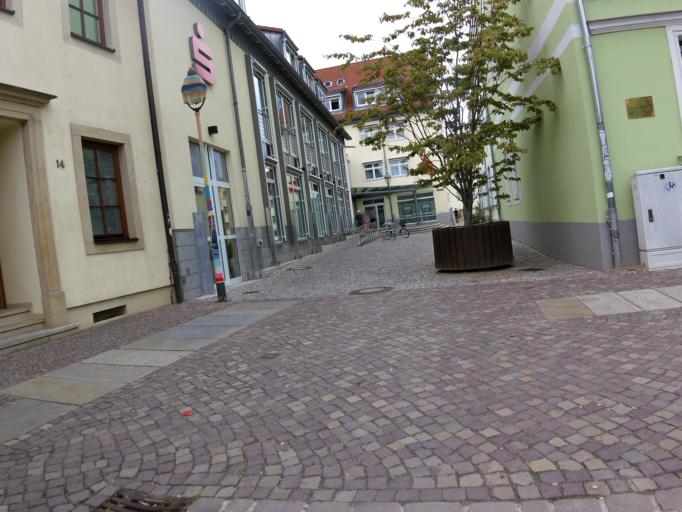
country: DE
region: Saxony
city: Dobeln
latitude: 51.1216
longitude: 13.1187
